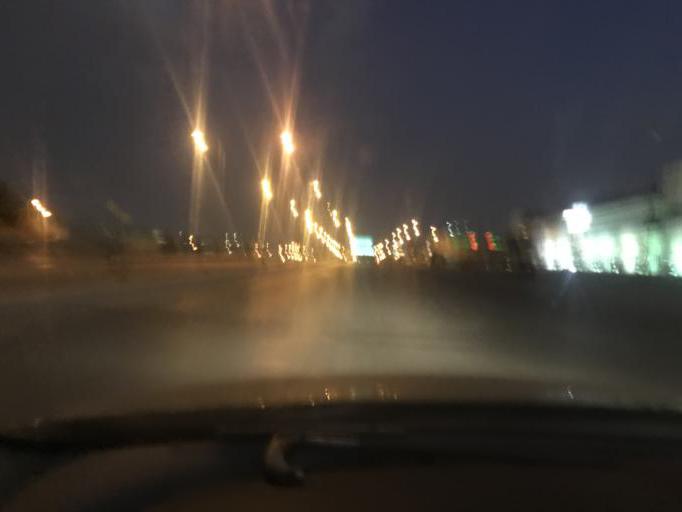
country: SA
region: Ar Riyad
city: Riyadh
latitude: 24.8089
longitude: 46.6922
